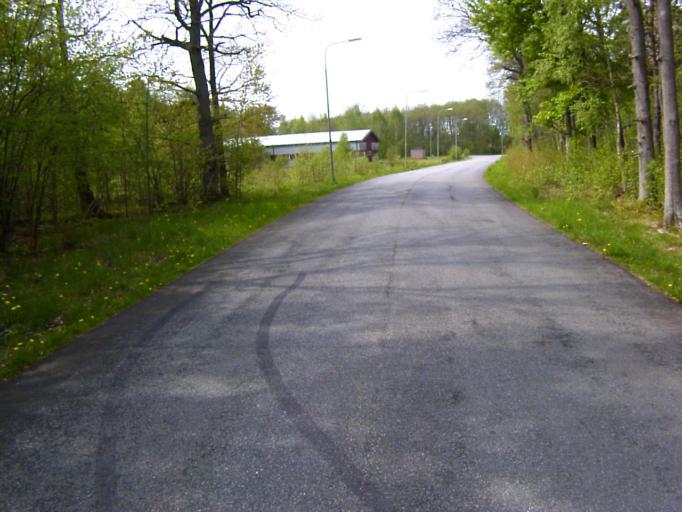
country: SE
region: Skane
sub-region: Kristianstads Kommun
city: Onnestad
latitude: 55.9335
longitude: 13.9933
